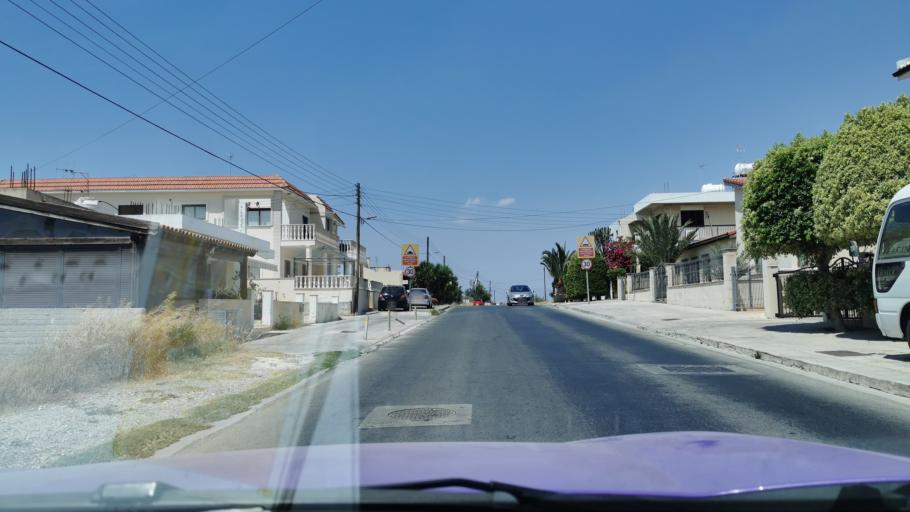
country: CY
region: Lefkosia
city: Kato Deftera
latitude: 35.1190
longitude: 33.2923
